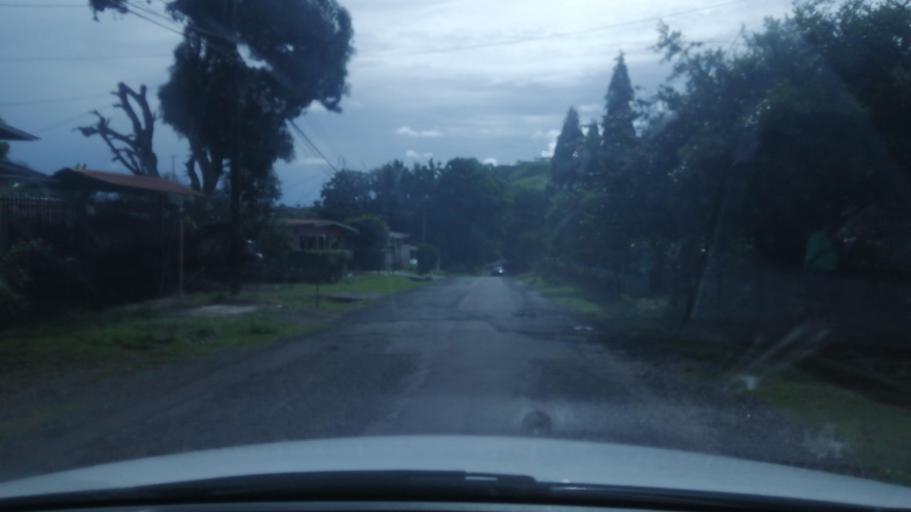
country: PA
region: Chiriqui
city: David
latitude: 8.4064
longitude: -82.4367
